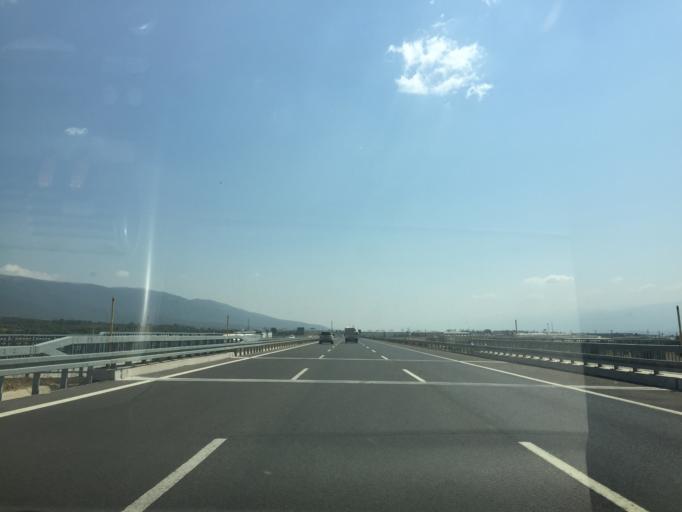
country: TR
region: Izmir
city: Kemalpasa
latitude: 38.4695
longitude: 27.3664
